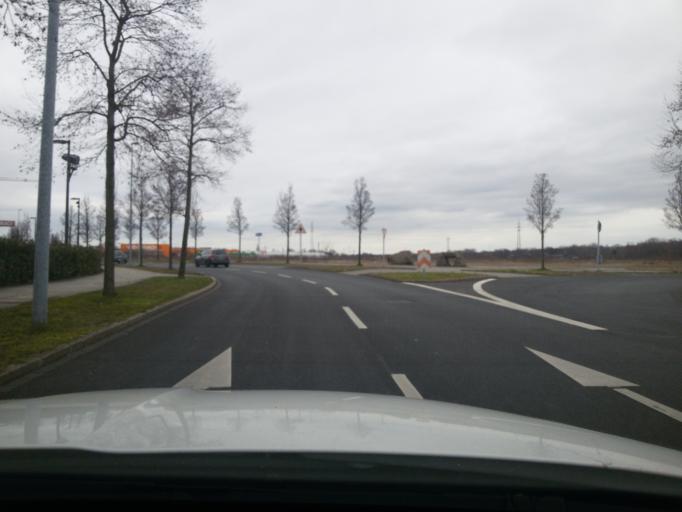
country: DE
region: North Rhine-Westphalia
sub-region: Regierungsbezirk Dusseldorf
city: Oberhausen
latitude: 51.4872
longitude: 6.8830
